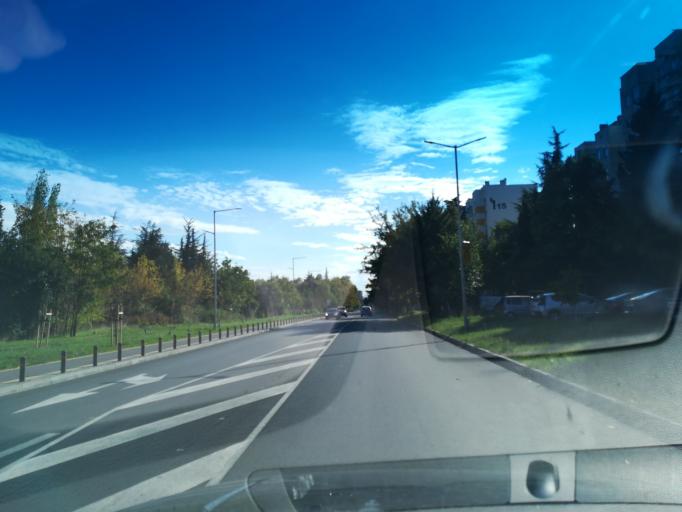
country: BG
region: Stara Zagora
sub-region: Obshtina Stara Zagora
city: Stara Zagora
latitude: 42.4382
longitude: 25.6358
